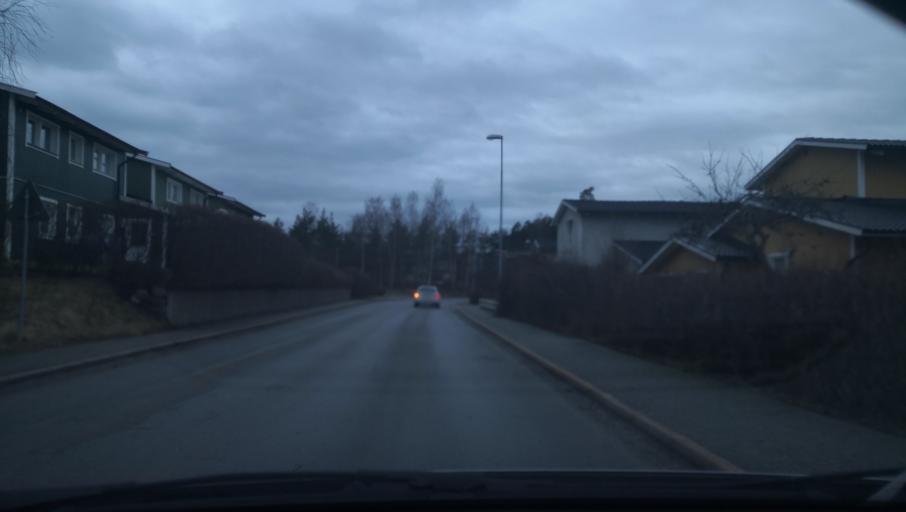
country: SE
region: Stockholm
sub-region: Taby Kommun
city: Taby
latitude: 59.4655
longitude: 18.0365
